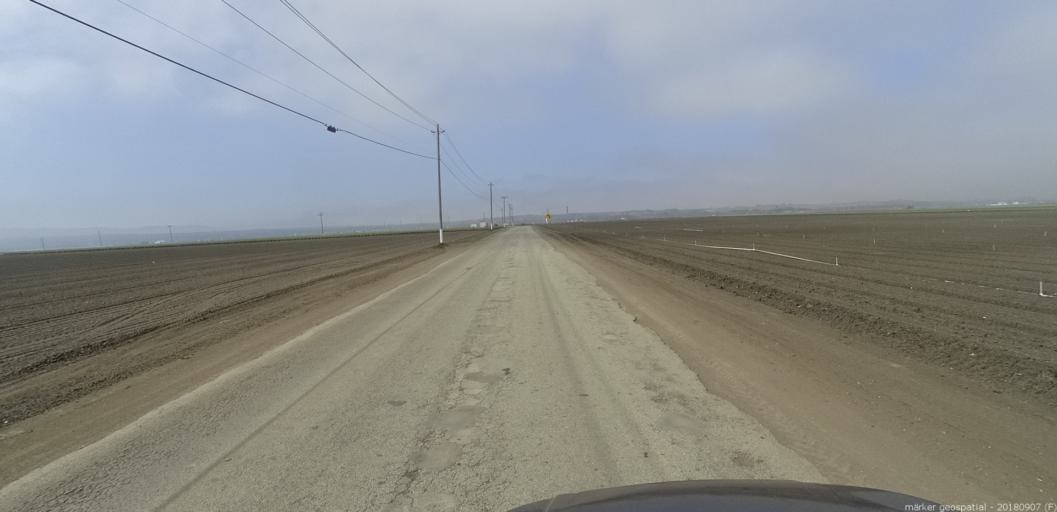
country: US
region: California
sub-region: Monterey County
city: Boronda
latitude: 36.7091
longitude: -121.7281
